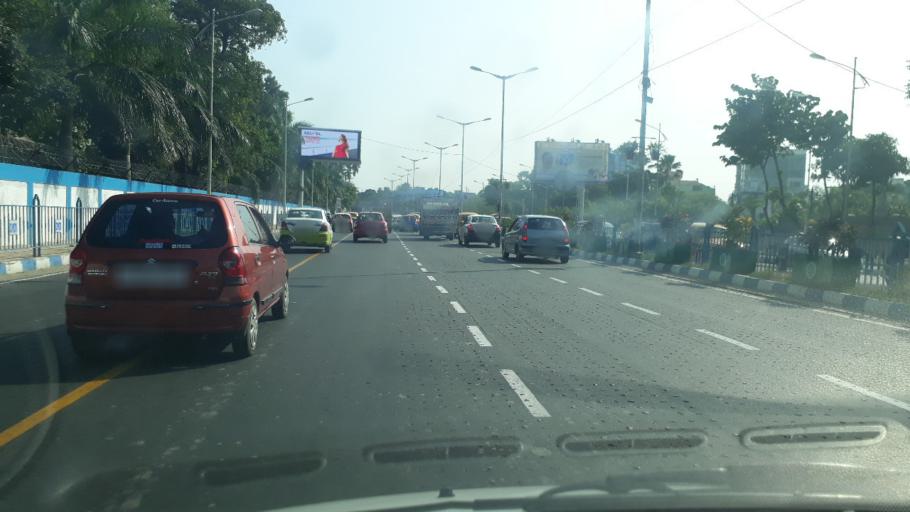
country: IN
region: West Bengal
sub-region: Kolkata
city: Kolkata
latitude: 22.5640
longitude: 88.4074
